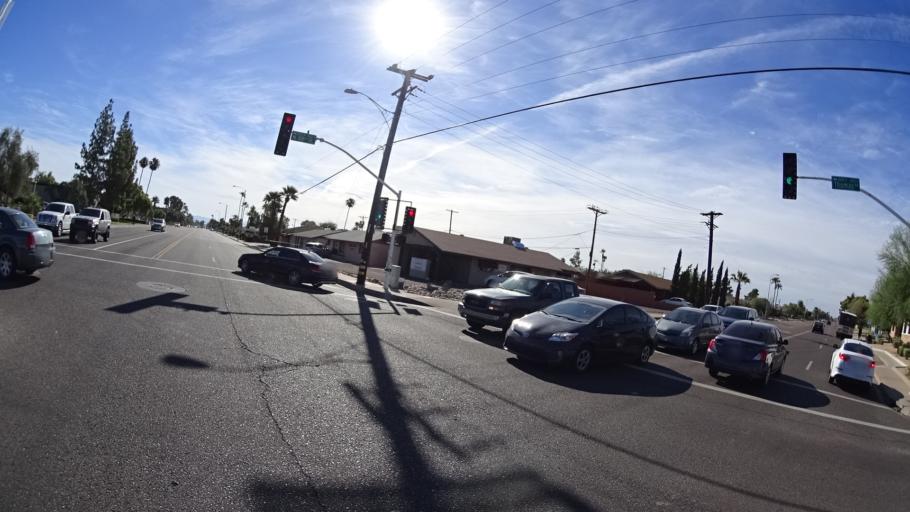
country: US
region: Arizona
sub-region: Maricopa County
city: Scottsdale
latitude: 33.4803
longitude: -111.9348
